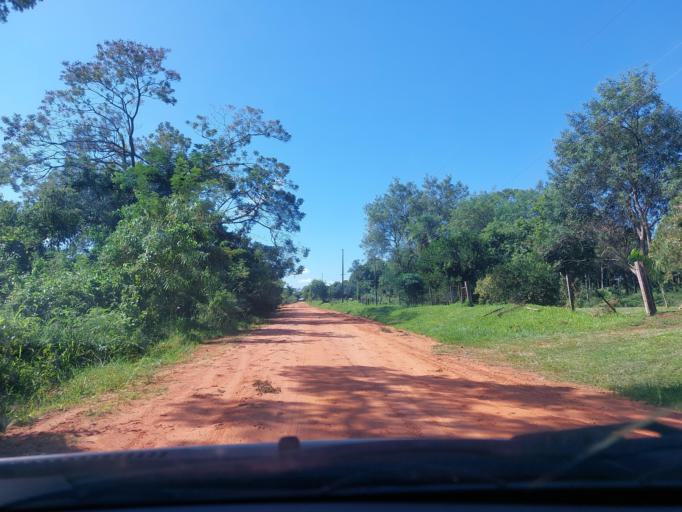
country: PY
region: San Pedro
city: Itacurubi del Rosario
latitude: -24.5376
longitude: -56.5797
